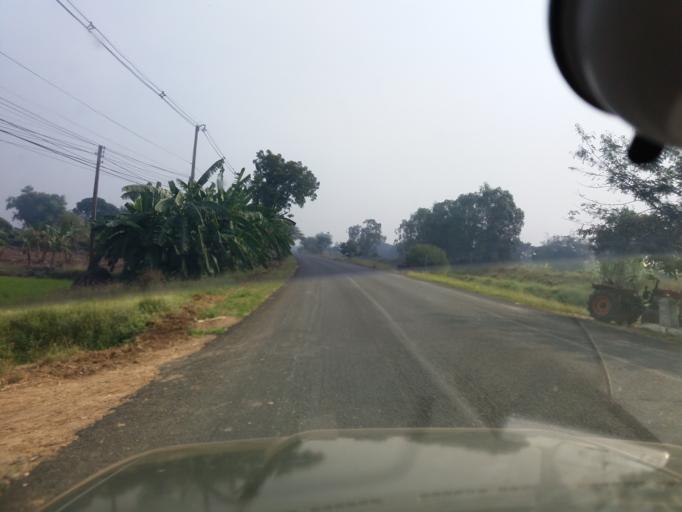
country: TH
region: Sing Buri
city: Bang Racham
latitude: 14.9062
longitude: 100.2032
